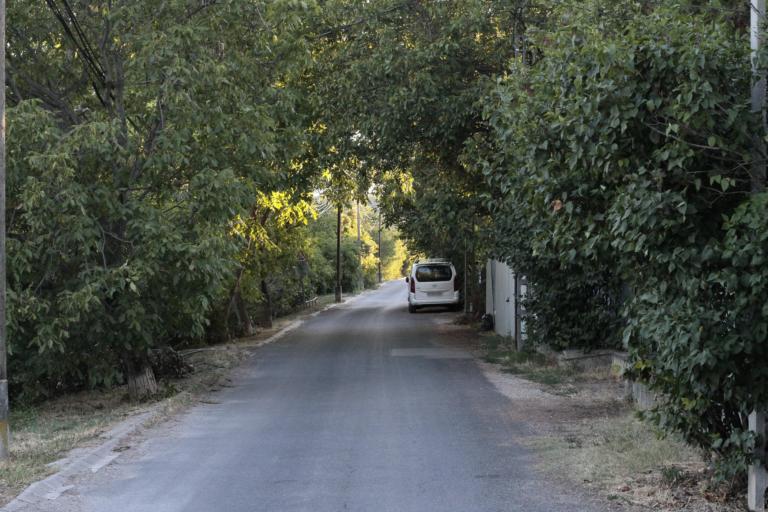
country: HU
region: Pest
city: Diosd
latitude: 47.4123
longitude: 18.9467
